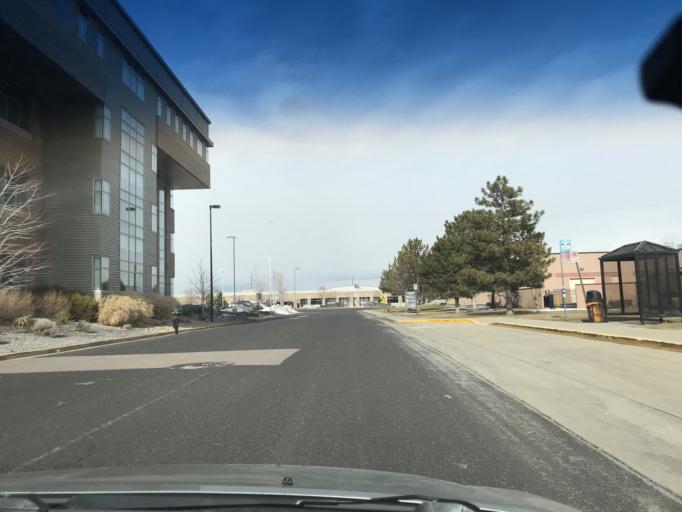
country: US
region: Utah
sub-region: Salt Lake County
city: Salt Lake City
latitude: 40.7743
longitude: -111.9474
